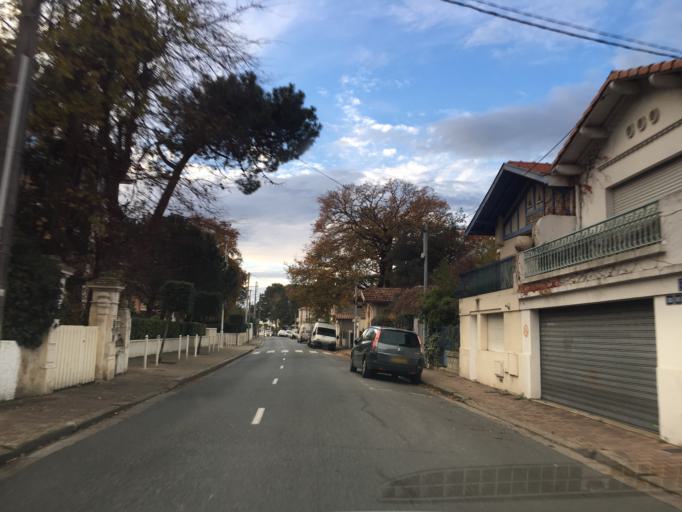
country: FR
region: Aquitaine
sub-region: Departement de la Gironde
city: Arcachon
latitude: 44.6627
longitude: -1.1609
